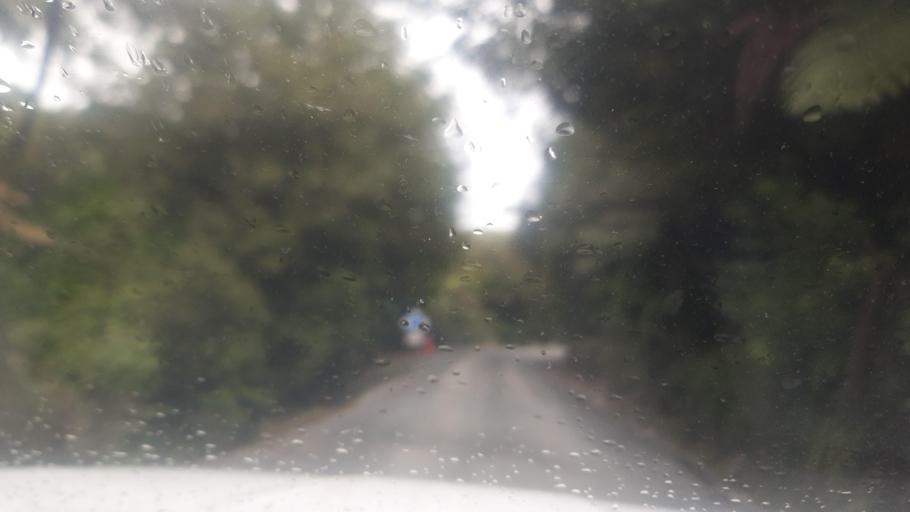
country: NZ
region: Northland
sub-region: Far North District
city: Taipa
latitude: -35.0933
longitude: 173.3951
